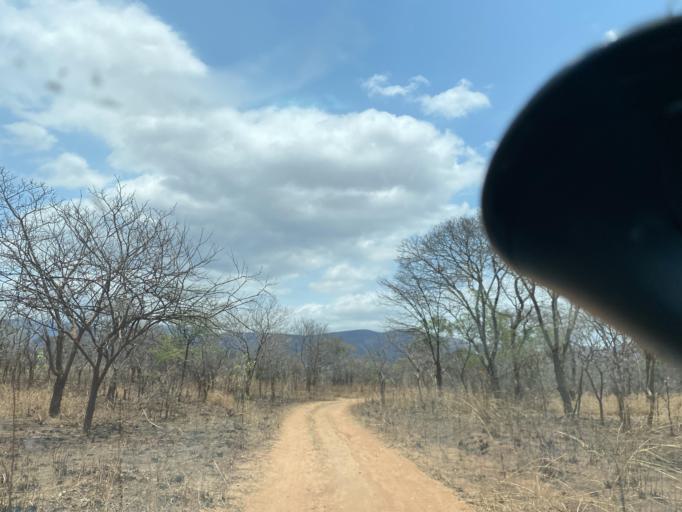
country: ZM
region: Lusaka
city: Luangwa
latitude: -15.1771
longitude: 29.7133
